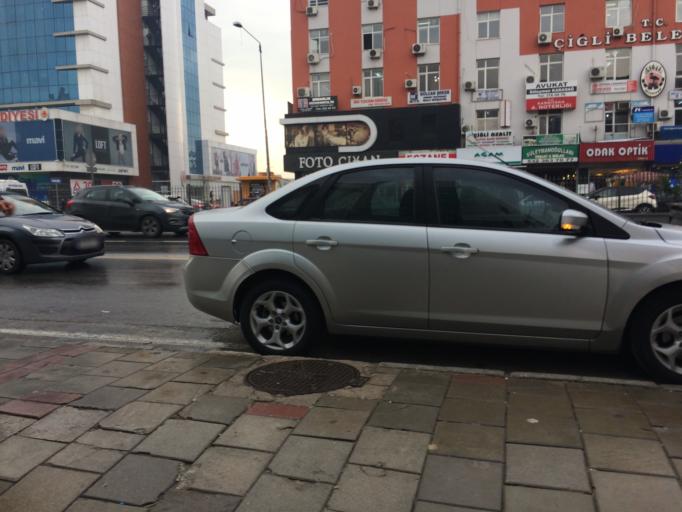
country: TR
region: Izmir
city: Karsiyaka
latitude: 38.4922
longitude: 27.0650
